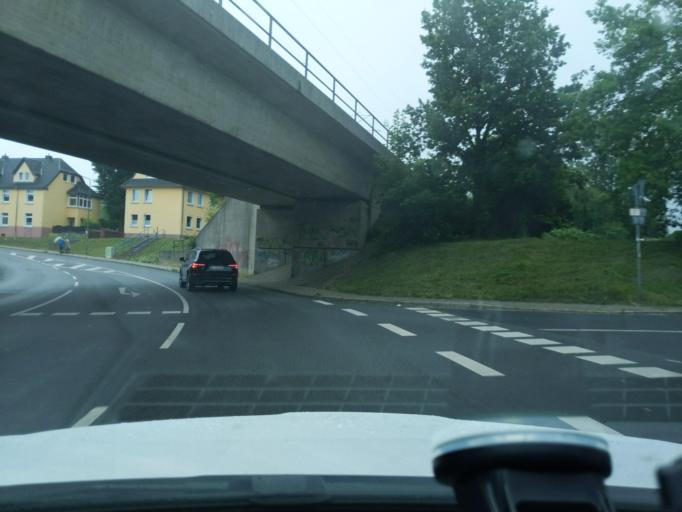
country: DE
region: North Rhine-Westphalia
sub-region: Regierungsbezirk Dusseldorf
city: Ratingen
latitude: 51.2871
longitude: 6.8577
